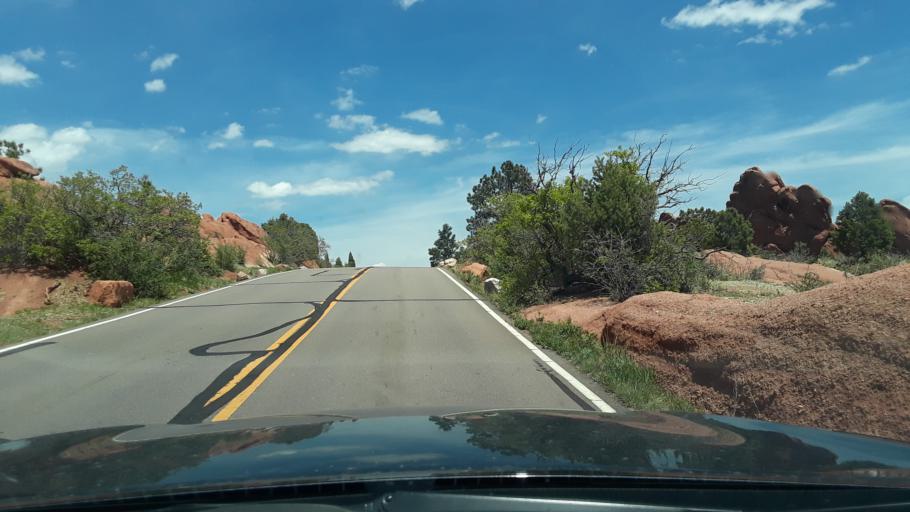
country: US
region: Colorado
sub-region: El Paso County
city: Manitou Springs
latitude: 38.8638
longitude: -104.8784
